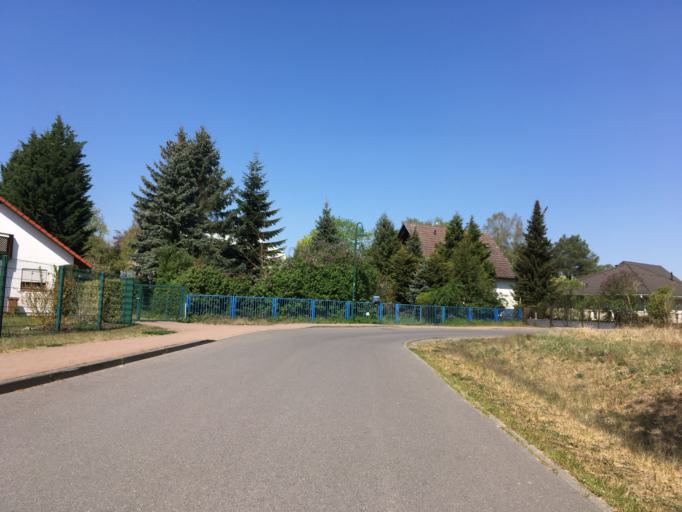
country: DE
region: Berlin
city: Buch
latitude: 52.6636
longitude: 13.5340
